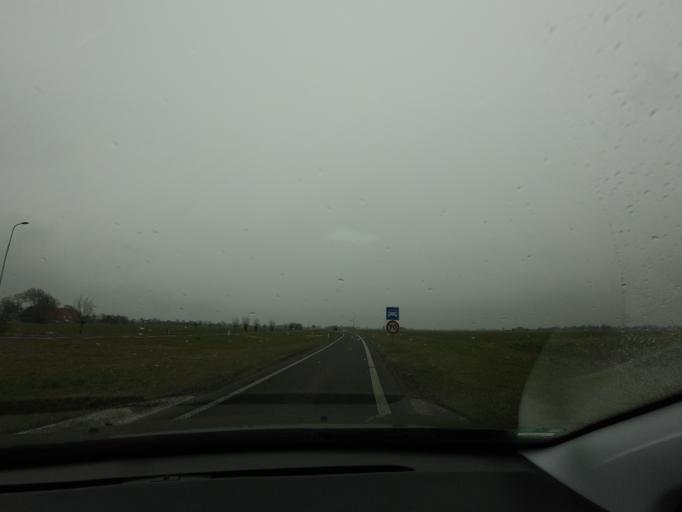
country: NL
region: Friesland
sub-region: Gemeente Littenseradiel
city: Wommels
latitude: 53.1242
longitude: 5.5929
